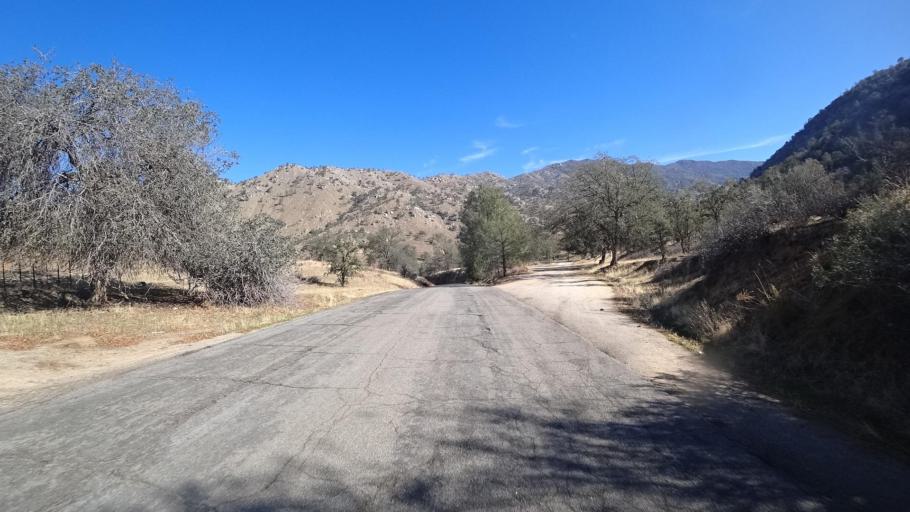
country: US
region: California
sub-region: Kern County
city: Bodfish
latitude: 35.5328
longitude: -118.6199
